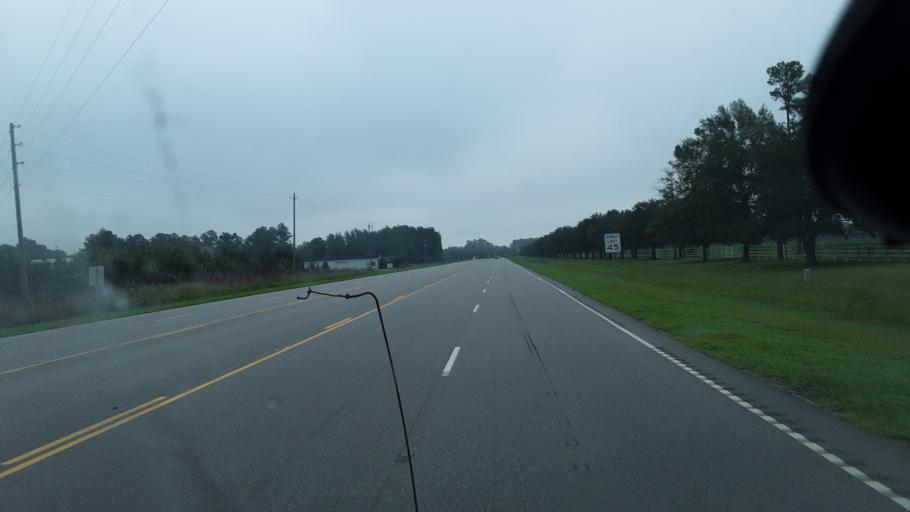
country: US
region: South Carolina
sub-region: Florence County
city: Johnsonville
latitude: 33.8821
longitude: -79.4636
